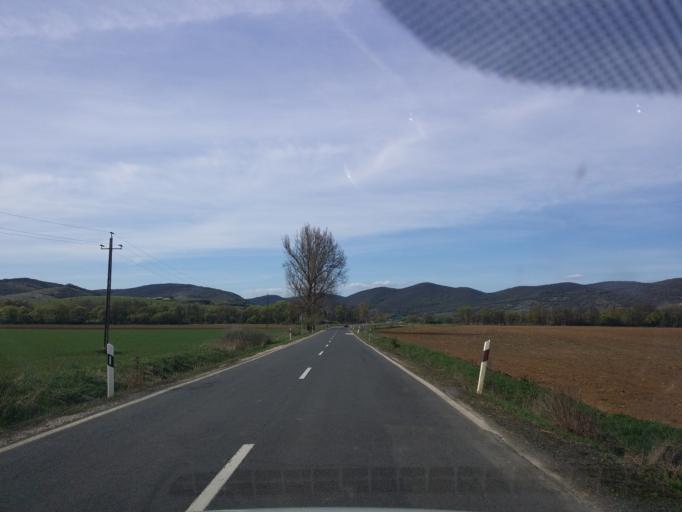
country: HU
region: Borsod-Abauj-Zemplen
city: Szendro
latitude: 48.4931
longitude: 20.6917
